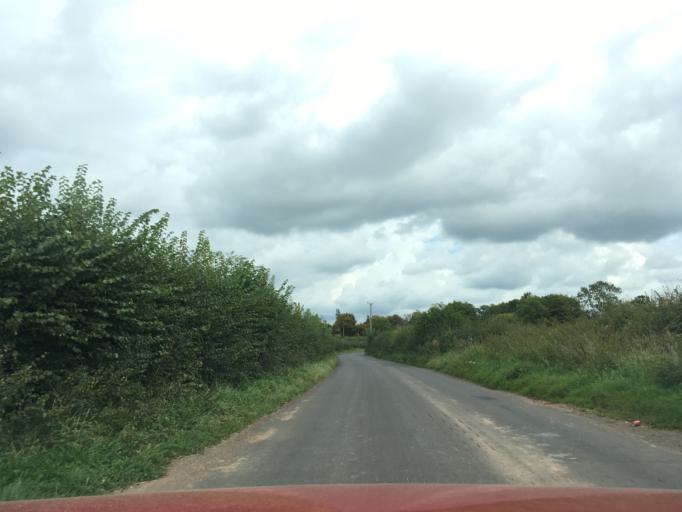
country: GB
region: England
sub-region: Gloucestershire
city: Berkeley
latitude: 51.6811
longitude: -2.4694
